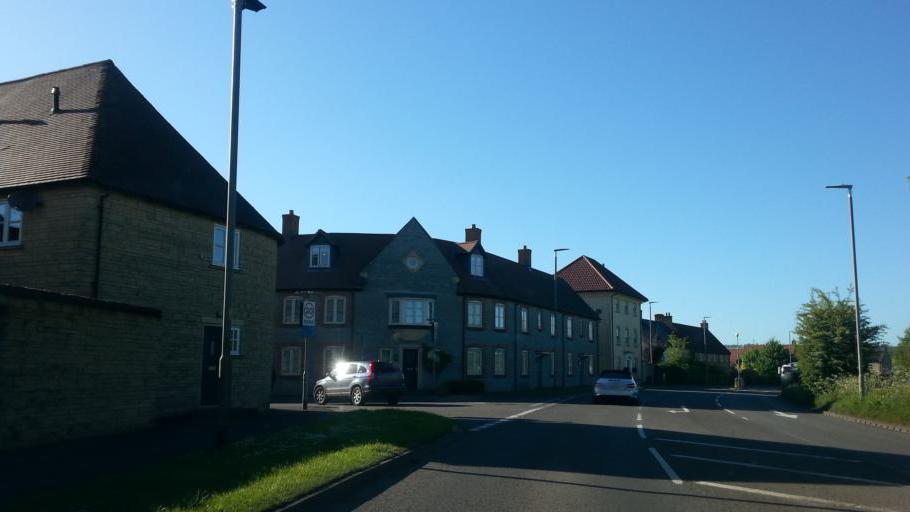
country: GB
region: England
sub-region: Somerset
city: Shepton Mallet
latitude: 51.1806
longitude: -2.5360
